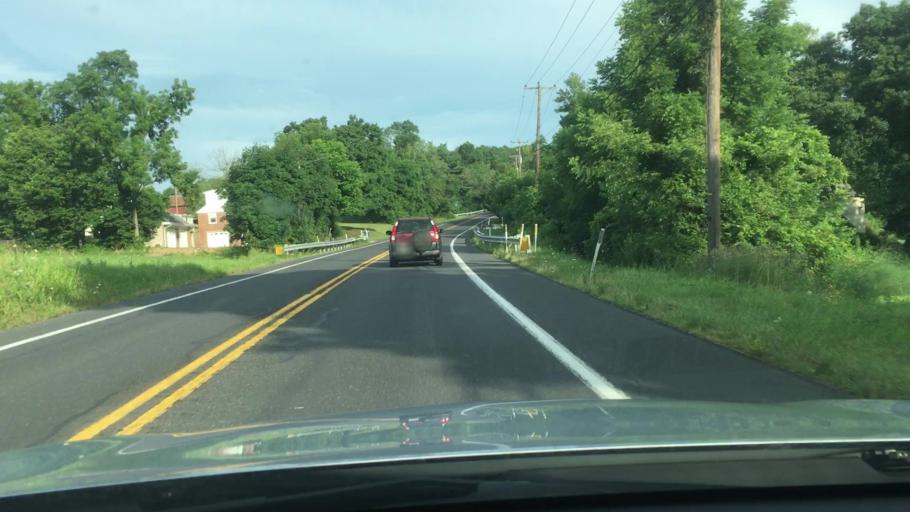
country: US
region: Pennsylvania
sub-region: York County
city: Dover
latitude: 40.0345
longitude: -76.8819
